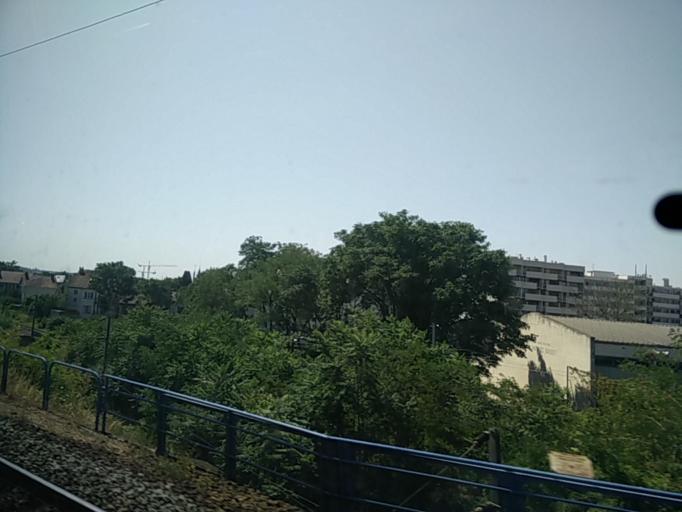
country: FR
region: Ile-de-France
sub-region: Departement du Val-de-Marne
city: Champigny-sur-Marne
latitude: 48.8265
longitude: 2.5029
